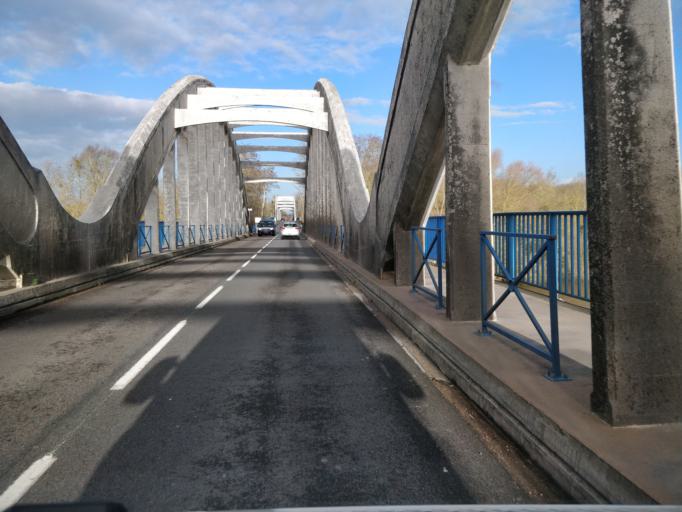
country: FR
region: Centre
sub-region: Departement du Loir-et-Cher
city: Muides-sur-Loire
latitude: 47.6752
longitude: 1.5266
